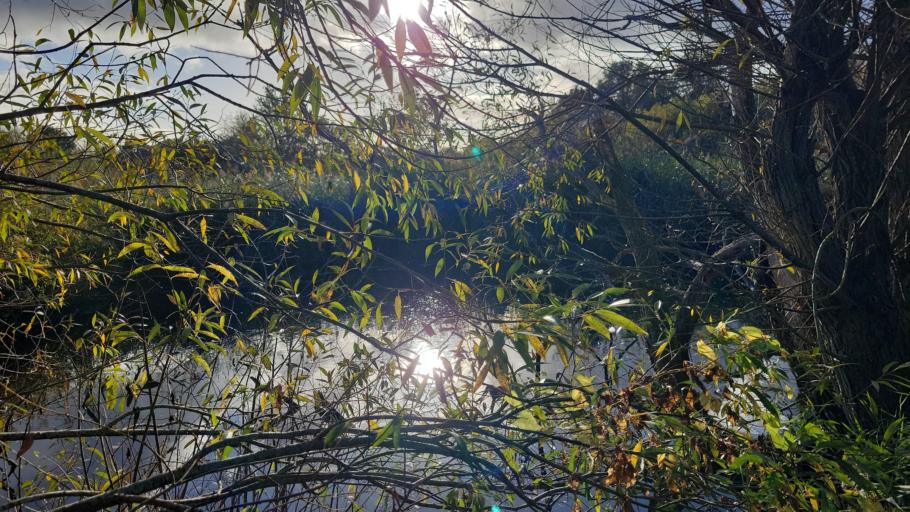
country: DK
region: Capital Region
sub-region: Egedal Kommune
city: Smorumnedre
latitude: 55.7579
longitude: 12.2938
